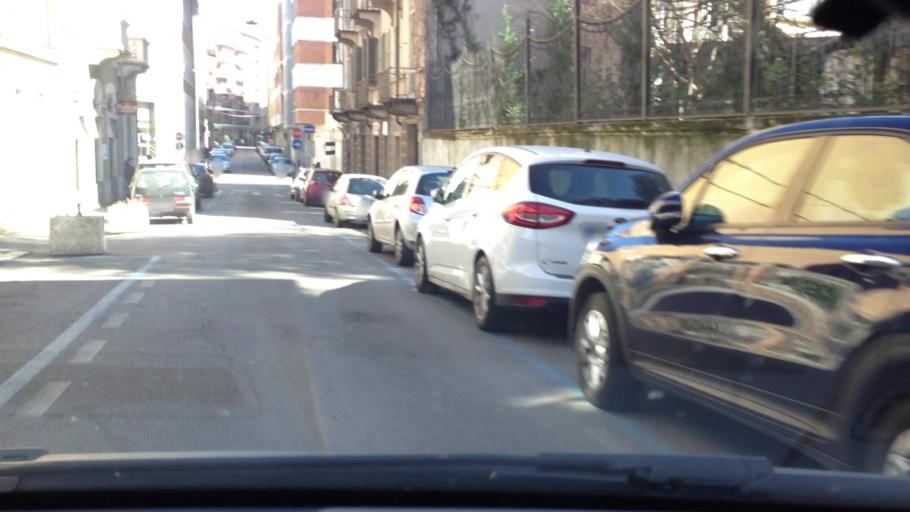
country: IT
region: Piedmont
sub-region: Provincia di Asti
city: Asti
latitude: 44.9042
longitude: 8.2065
